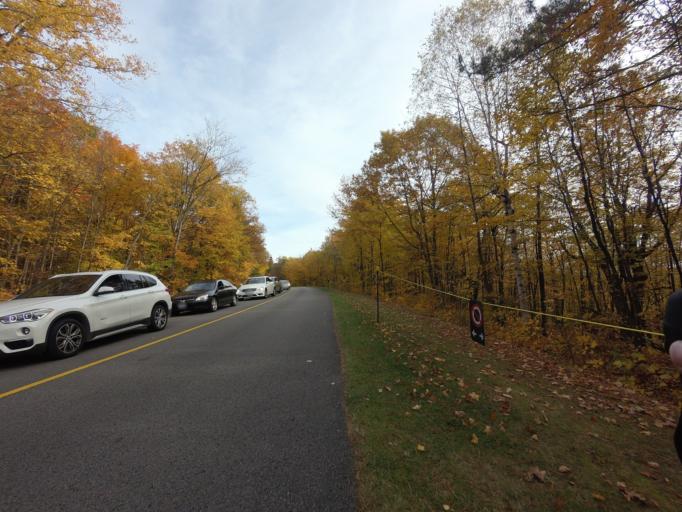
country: CA
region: Quebec
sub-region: Outaouais
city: Gatineau
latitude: 45.4662
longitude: -75.8130
